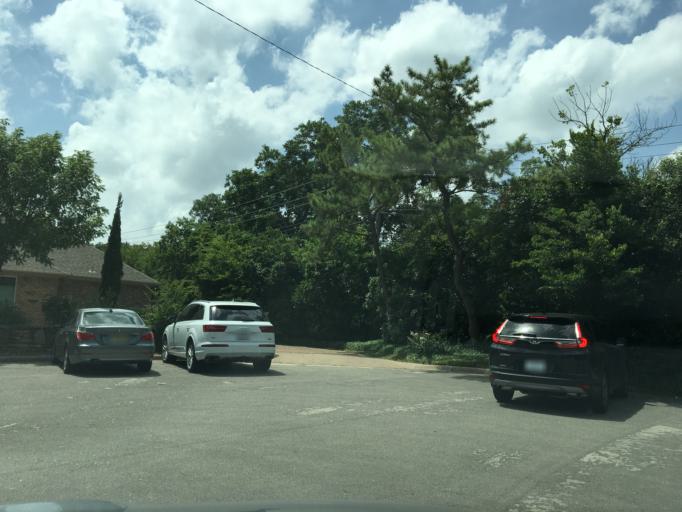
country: US
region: Texas
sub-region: Dallas County
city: University Park
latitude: 32.8967
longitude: -96.7822
